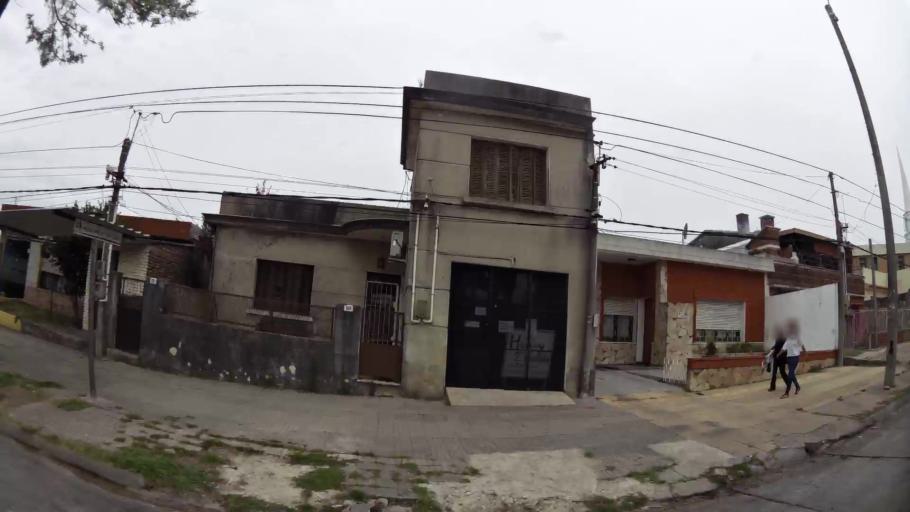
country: UY
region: Canelones
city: Las Piedras
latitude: -34.7265
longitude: -56.2079
